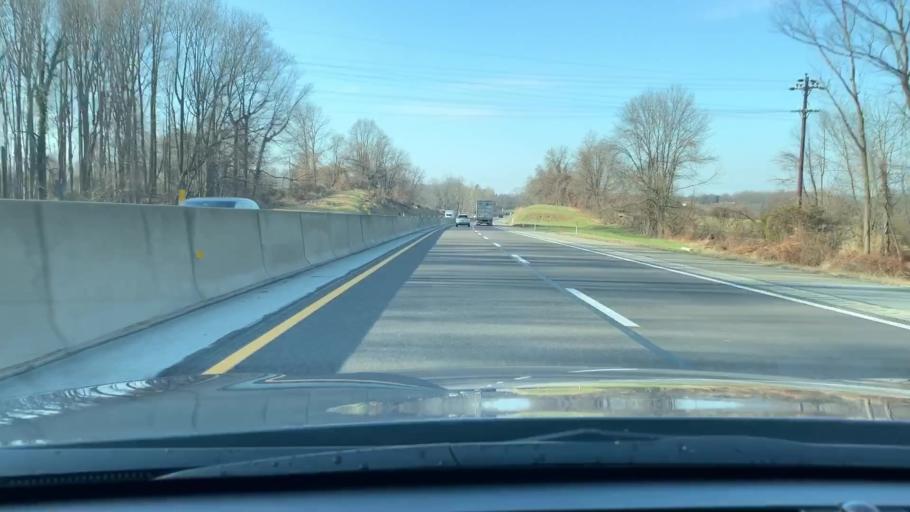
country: US
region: Pennsylvania
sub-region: Chester County
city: Chester Springs
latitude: 40.0648
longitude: -75.6011
